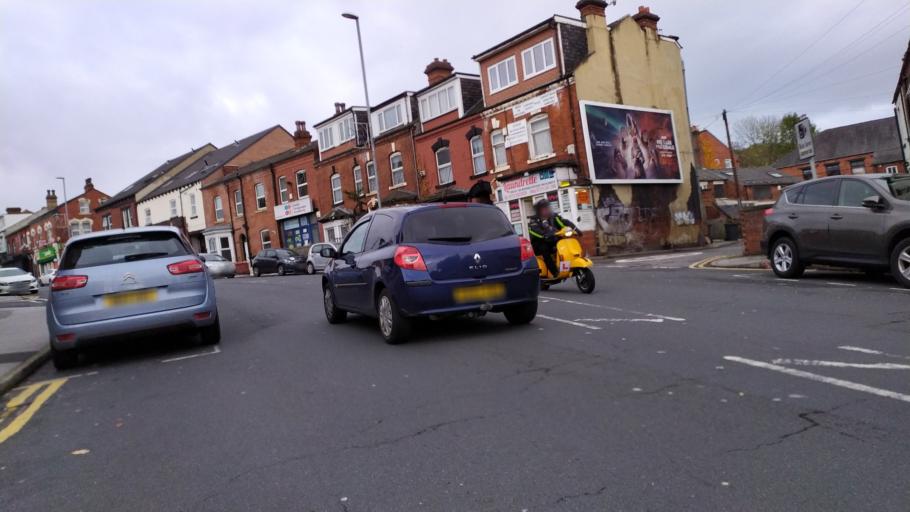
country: GB
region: England
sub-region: City and Borough of Leeds
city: Leeds
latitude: 53.8052
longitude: -1.5700
